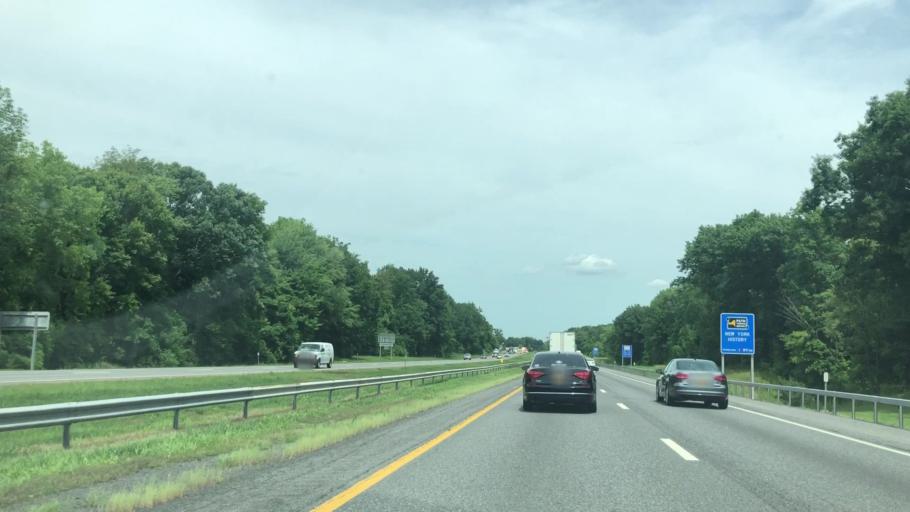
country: US
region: New York
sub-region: Albany County
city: Delmar
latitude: 42.6070
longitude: -73.7836
